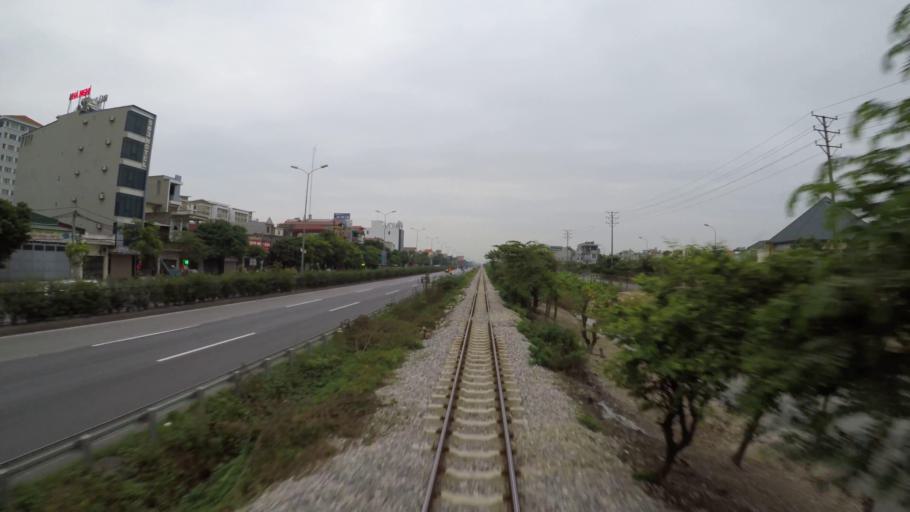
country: VN
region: Hung Yen
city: Nhu Quynh
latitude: 20.9835
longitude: 105.9792
